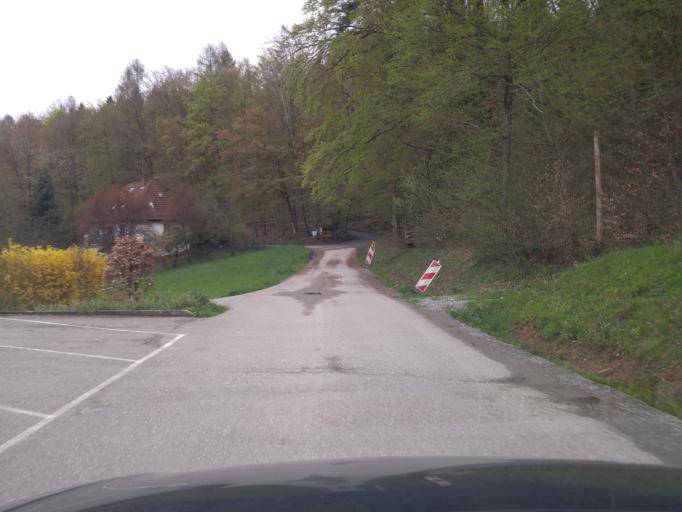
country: DE
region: Baden-Wuerttemberg
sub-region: Karlsruhe Region
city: Reichartshausen
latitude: 49.3821
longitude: 8.9624
